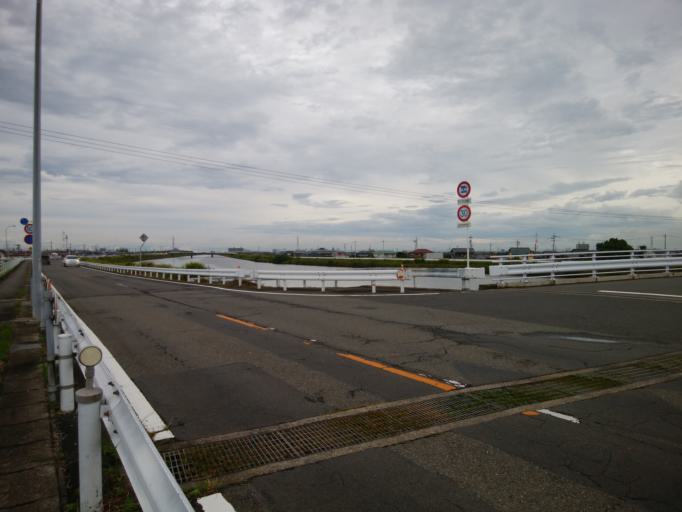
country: JP
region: Aichi
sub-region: Aisai-shi
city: Aisai
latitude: 35.1538
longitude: 136.7607
